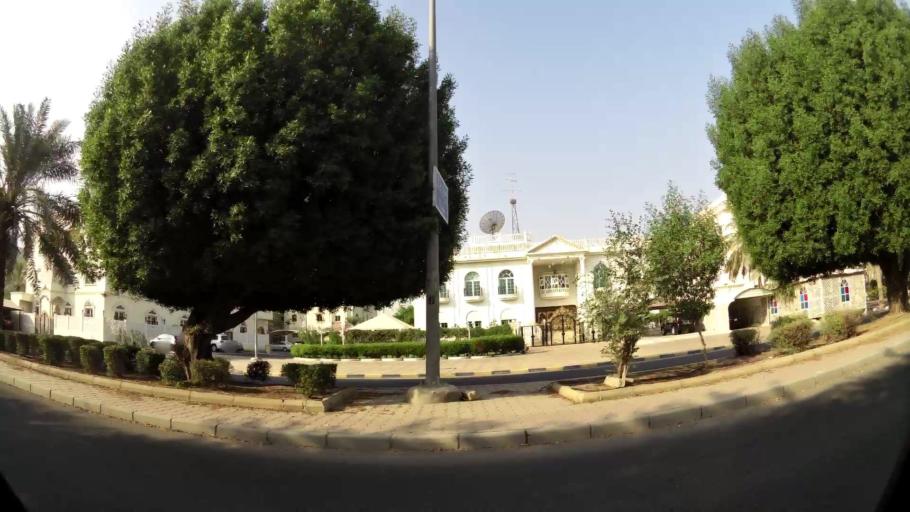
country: KW
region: Muhafazat Hawalli
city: Salwa
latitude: 29.2783
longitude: 48.0786
